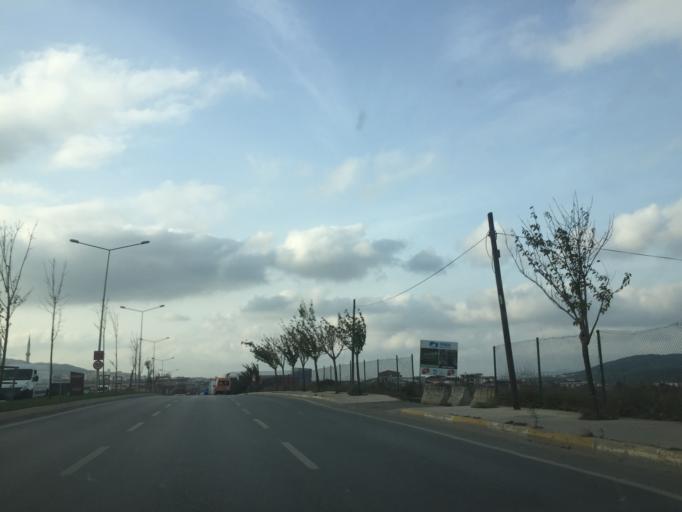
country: TR
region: Istanbul
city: Sultanbeyli
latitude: 40.9411
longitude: 29.3058
